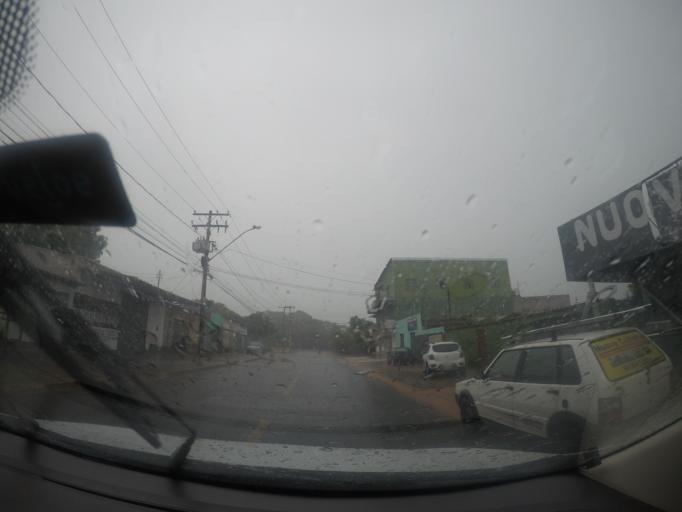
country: BR
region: Goias
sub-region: Goiania
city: Goiania
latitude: -16.6003
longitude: -49.3296
